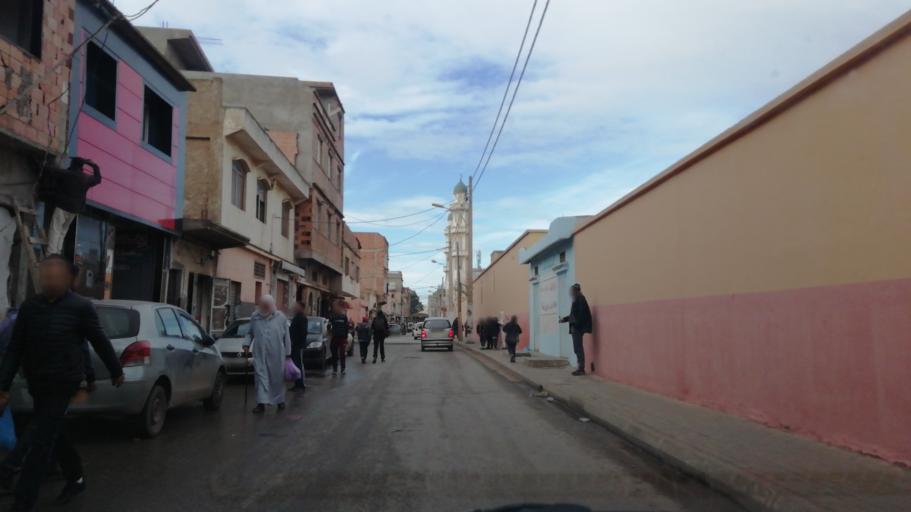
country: DZ
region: Oran
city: Oran
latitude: 35.6836
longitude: -0.5992
